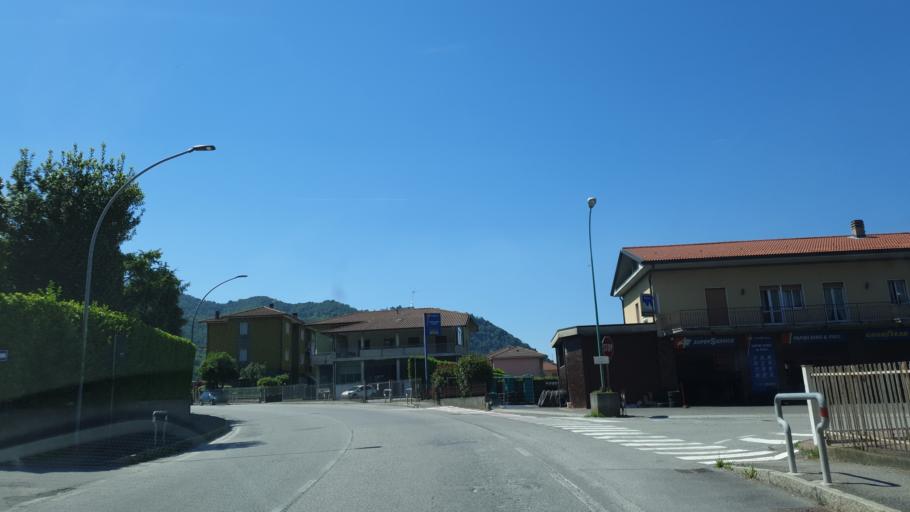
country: IT
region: Lombardy
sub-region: Provincia di Bergamo
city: Cisano Bergamasco
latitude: 45.7442
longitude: 9.4689
